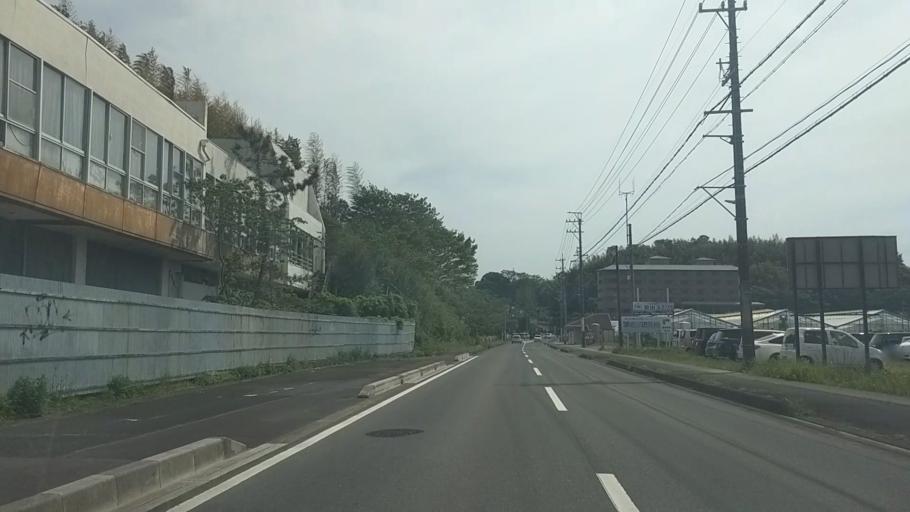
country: JP
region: Shizuoka
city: Kosai-shi
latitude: 34.7663
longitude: 137.6294
